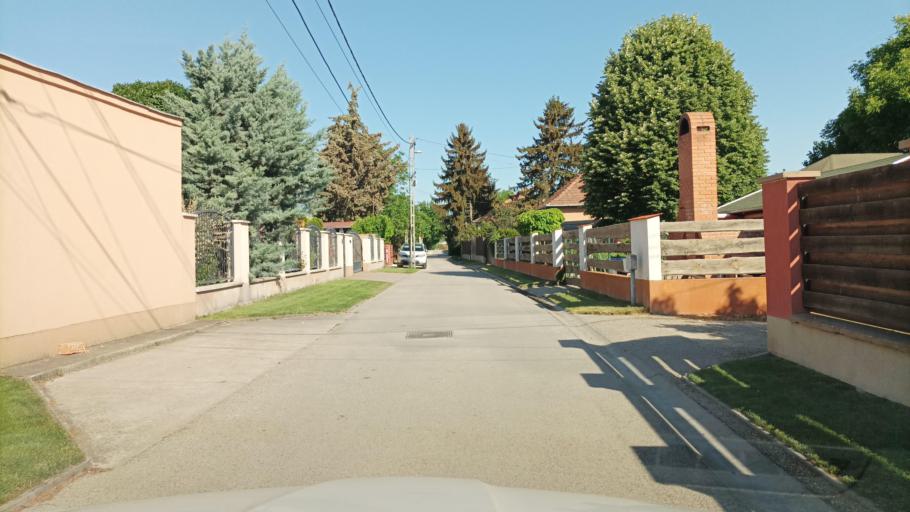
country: HU
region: Pest
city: Szigetszentmiklos
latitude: 47.3462
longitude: 19.0574
